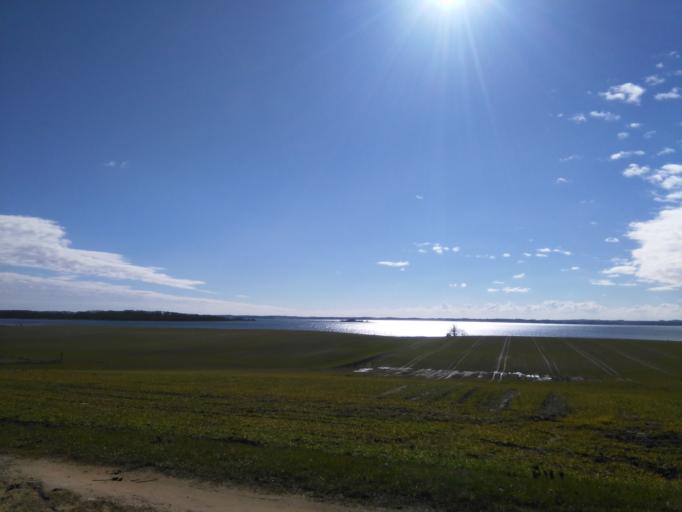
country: DK
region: Central Jutland
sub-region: Horsens Kommune
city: Horsens
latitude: 55.8841
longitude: 9.9801
